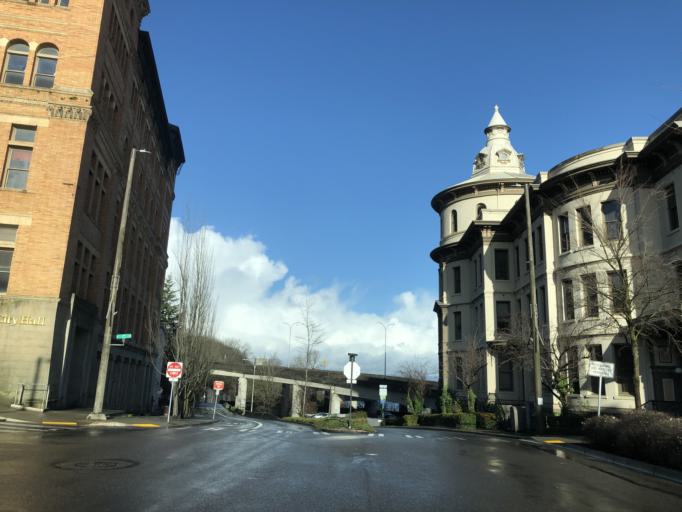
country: US
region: Washington
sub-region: Pierce County
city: Tacoma
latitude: 47.2572
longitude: -122.4396
